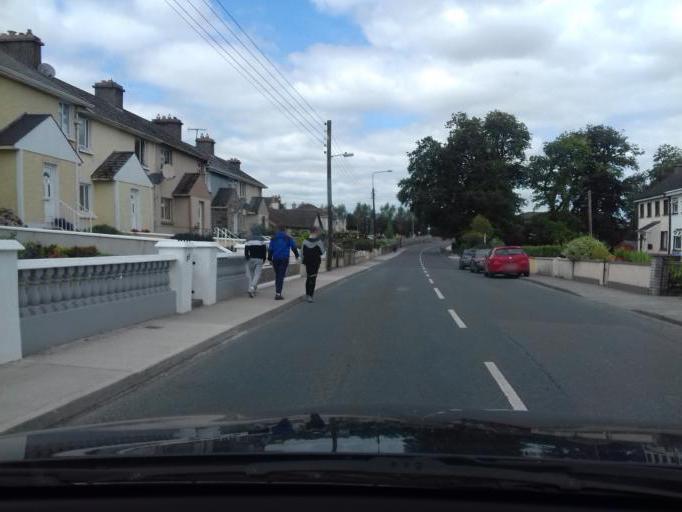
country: IE
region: Leinster
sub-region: County Carlow
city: Tullow
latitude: 52.8062
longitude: -6.7312
